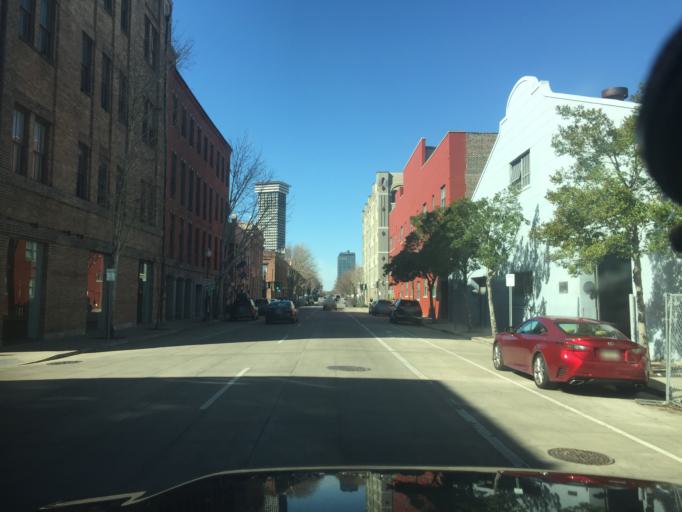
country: US
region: Louisiana
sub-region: Orleans Parish
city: New Orleans
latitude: 29.9451
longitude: -90.0682
